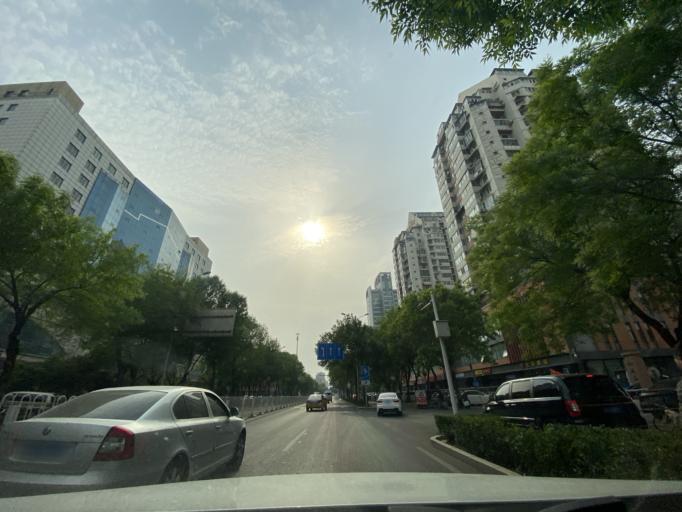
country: CN
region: Beijing
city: Haidian
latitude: 39.9752
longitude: 116.3410
